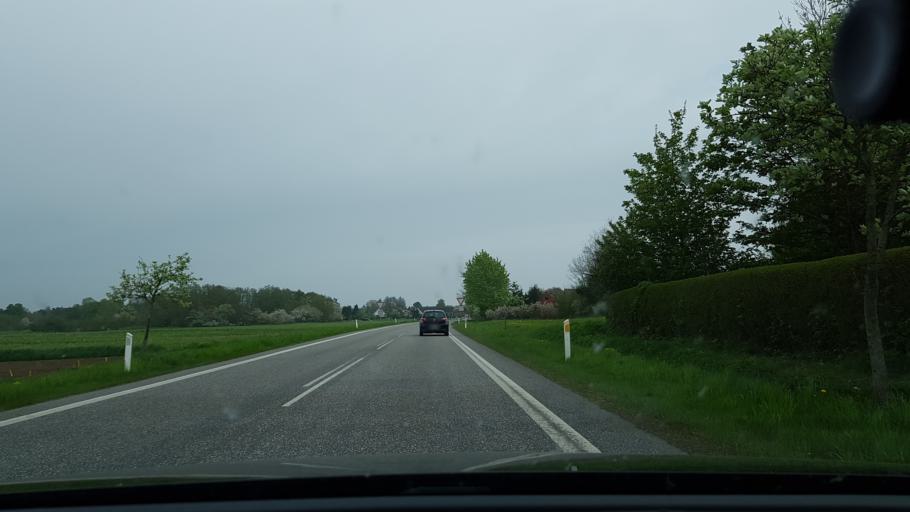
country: DK
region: Capital Region
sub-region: Bornholm Kommune
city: Nexo
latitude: 55.0254
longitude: 15.1043
